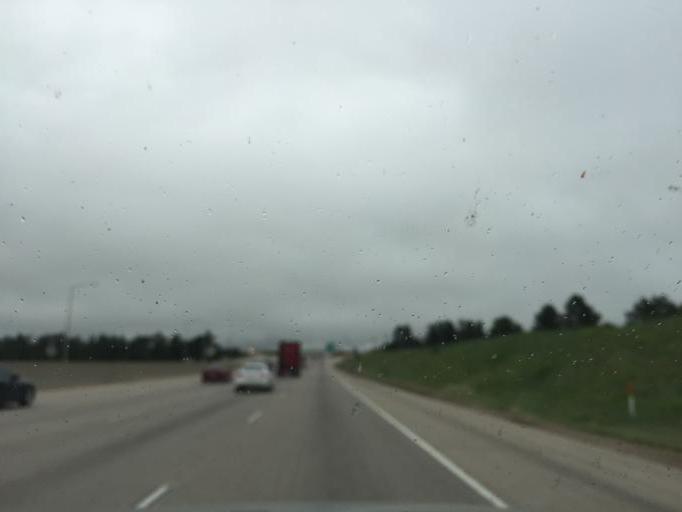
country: US
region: Colorado
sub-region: Douglas County
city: Castle Pines
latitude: 39.4437
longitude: -104.8754
